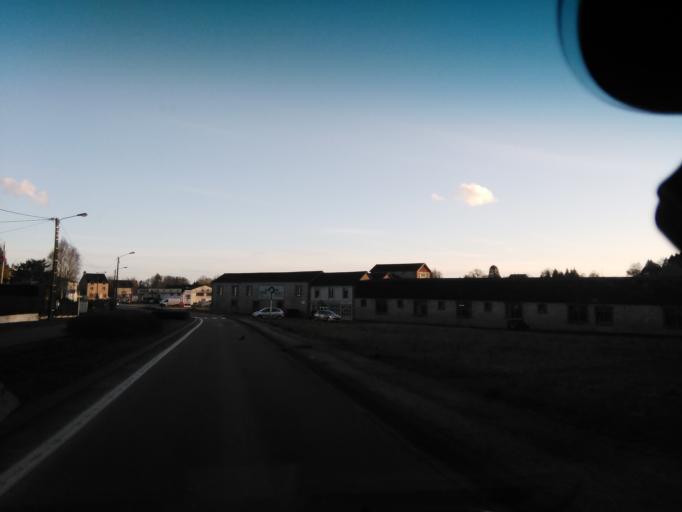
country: FR
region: Lower Normandy
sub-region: Departement de l'Orne
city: La Ferte-Mace
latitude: 48.5885
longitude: -0.3657
